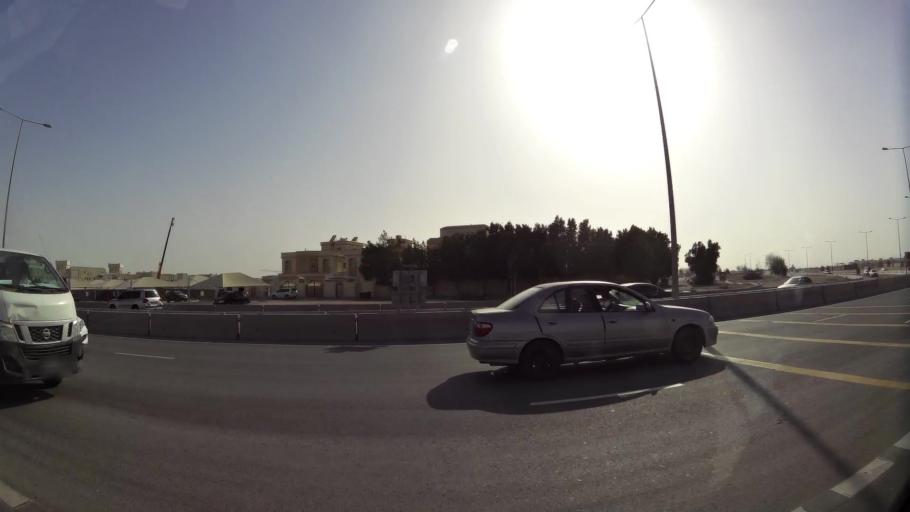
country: QA
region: Baladiyat ar Rayyan
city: Ar Rayyan
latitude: 25.3190
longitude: 51.4289
